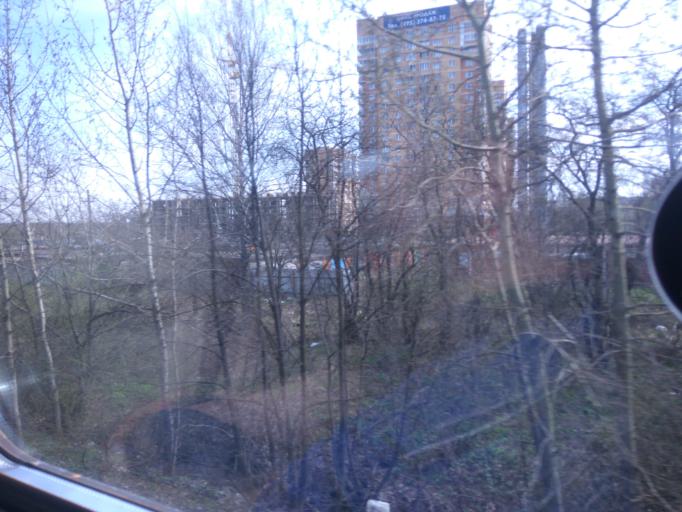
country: RU
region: Moskovskaya
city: Lobnya
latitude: 56.0245
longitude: 37.4858
